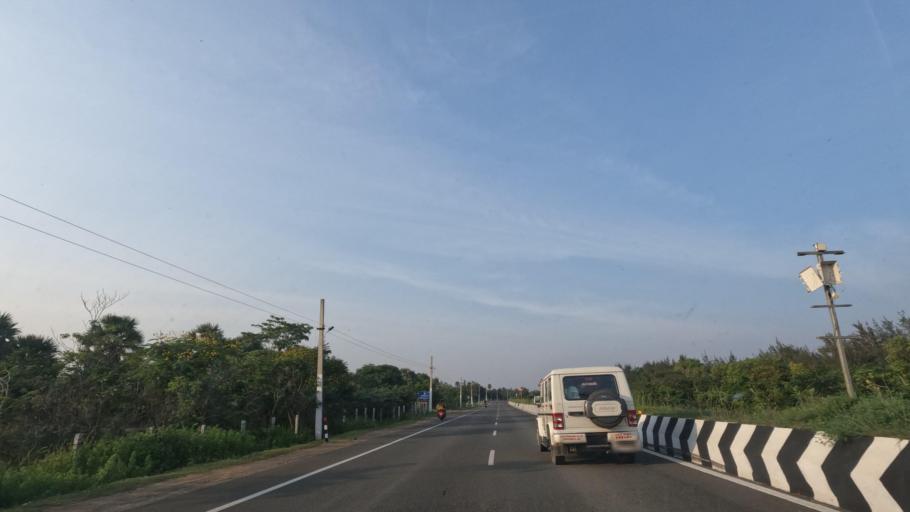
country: IN
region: Tamil Nadu
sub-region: Kancheepuram
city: Mamallapuram
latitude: 12.6652
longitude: 80.2096
